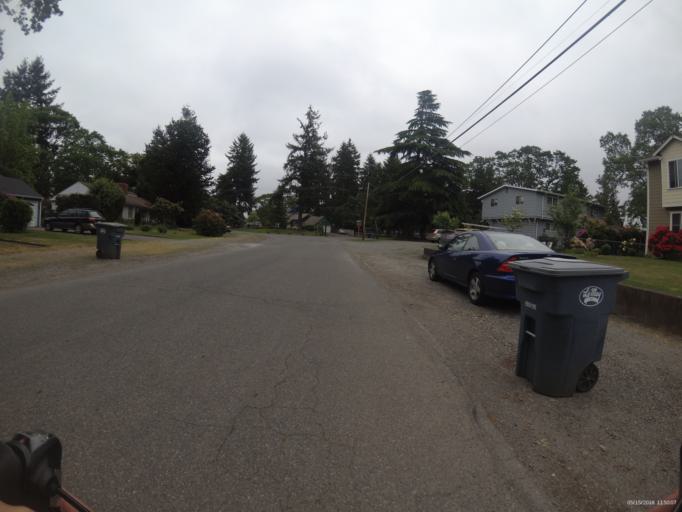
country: US
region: Washington
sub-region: Pierce County
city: Lakewood
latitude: 47.1752
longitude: -122.5227
